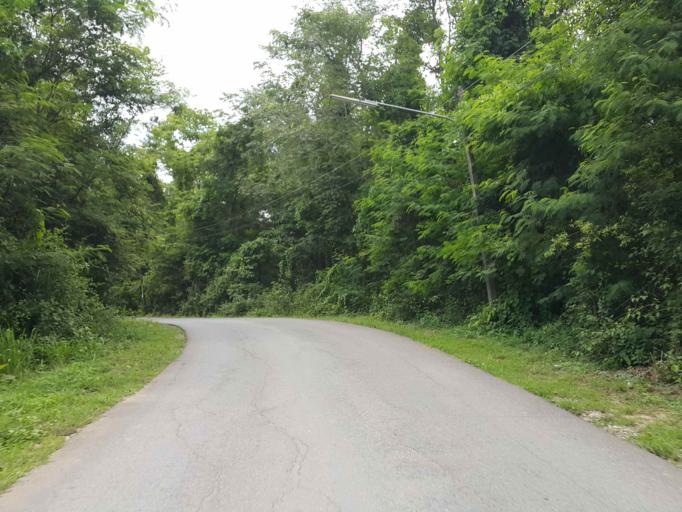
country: TH
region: Chiang Mai
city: San Sai
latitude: 18.9259
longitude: 98.9224
